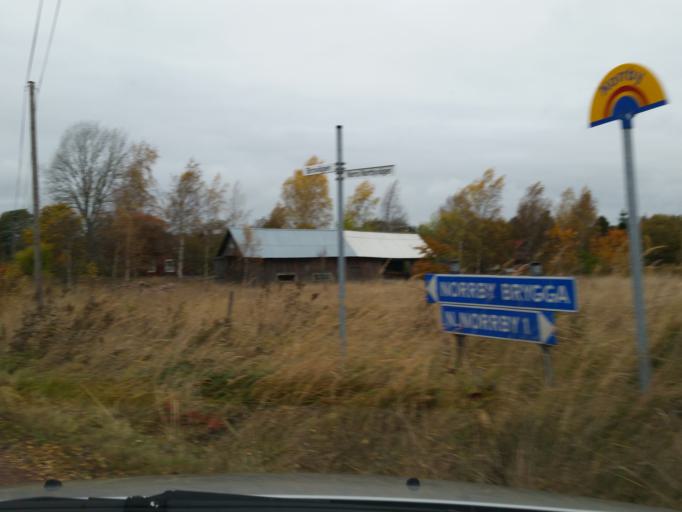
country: AX
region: Alands landsbygd
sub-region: Lemland
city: Lemland
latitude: 60.0786
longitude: 20.0821
